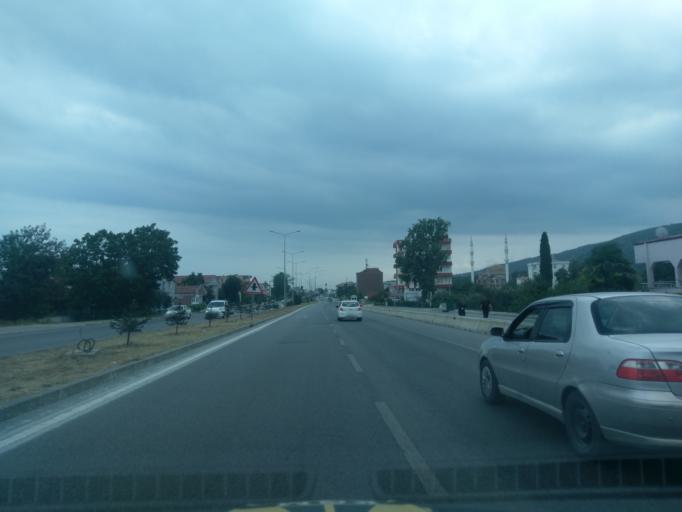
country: TR
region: Samsun
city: Taflan
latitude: 41.4051
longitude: 36.1834
